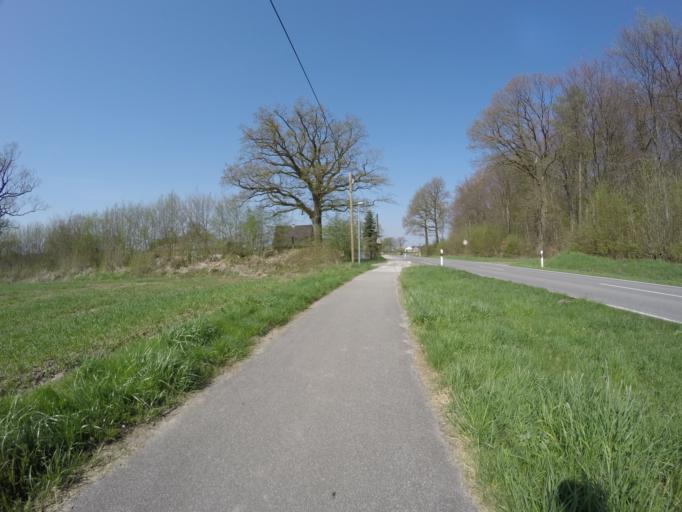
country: DE
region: Schleswig-Holstein
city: Bilsen
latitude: 53.7534
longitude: 9.8725
